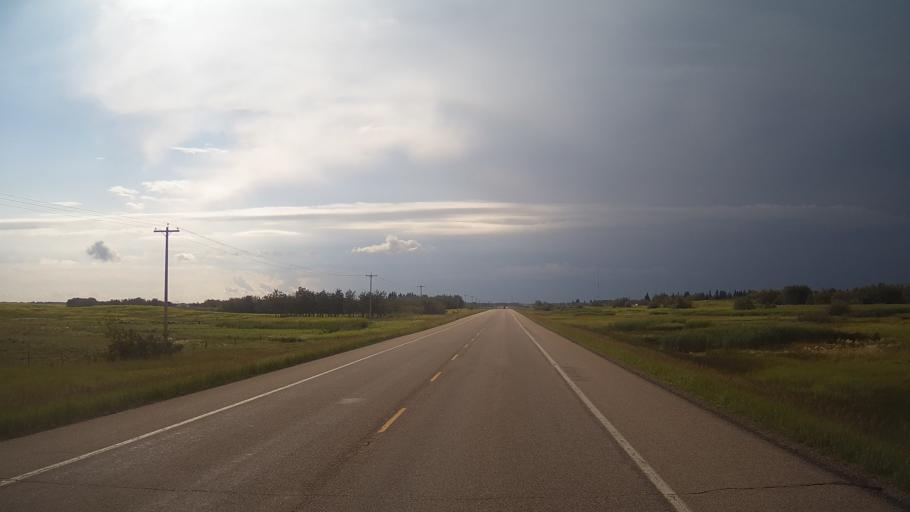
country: CA
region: Alberta
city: Viking
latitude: 53.1670
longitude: -112.0278
